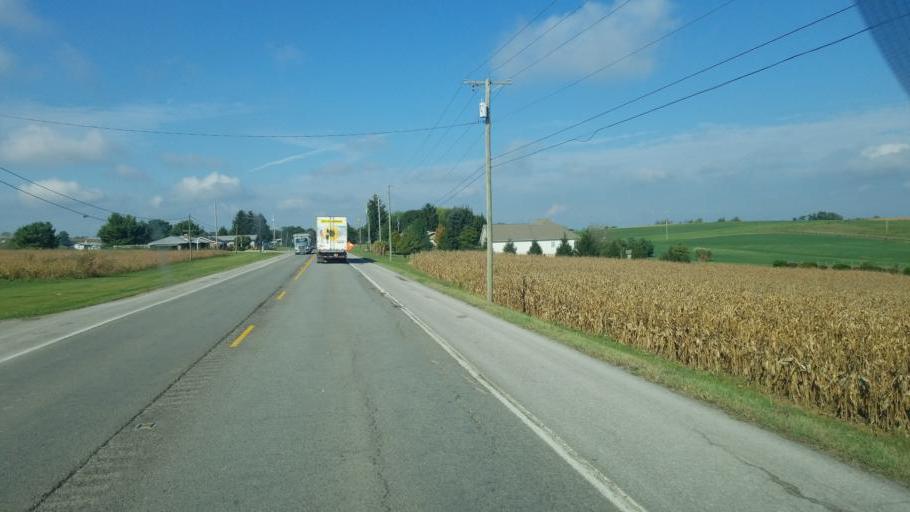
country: US
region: Ohio
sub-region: Stark County
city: Brewster
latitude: 40.6882
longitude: -81.6851
